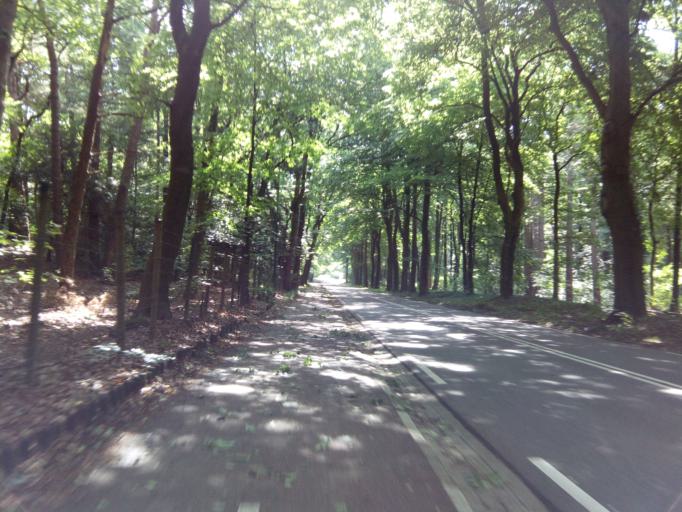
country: NL
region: Utrecht
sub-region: Gemeente Utrechtse Heuvelrug
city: Doorn
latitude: 52.0426
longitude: 5.3356
